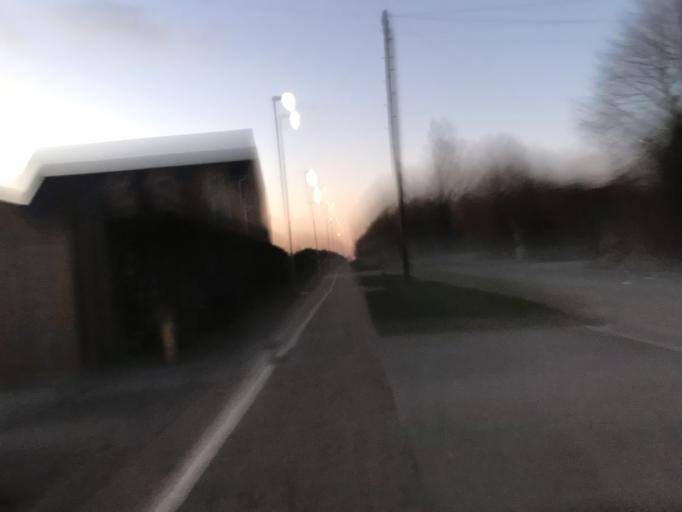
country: GB
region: England
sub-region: North East Lincolnshire
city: Waltham
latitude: 53.5245
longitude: -0.0782
